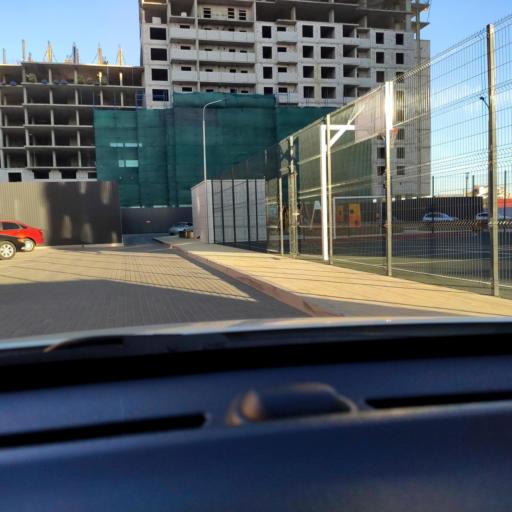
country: RU
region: Voronezj
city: Voronezh
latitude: 51.6538
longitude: 39.1943
